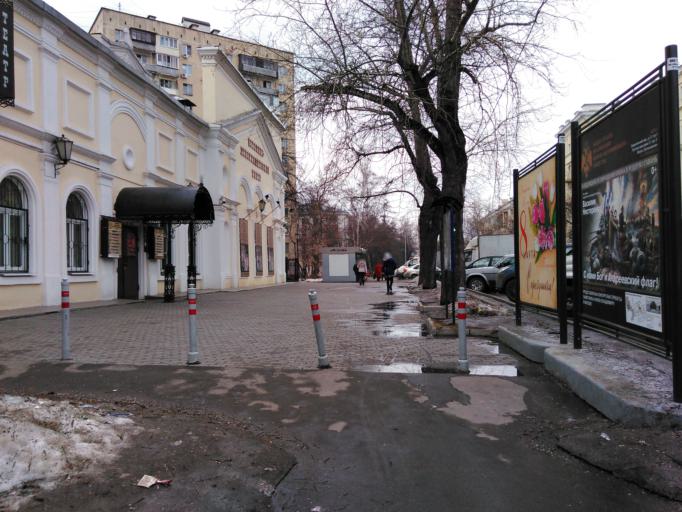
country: RU
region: Moscow
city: Vatutino
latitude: 55.8638
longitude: 37.6814
